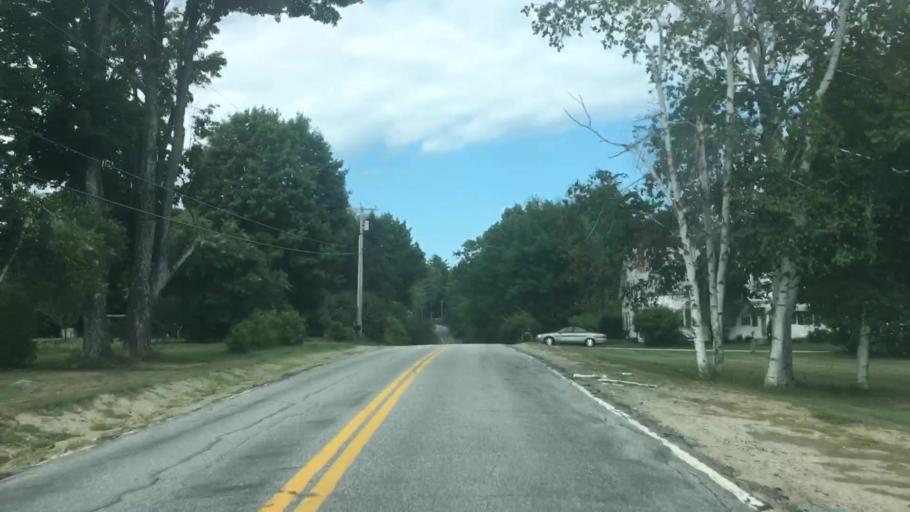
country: US
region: Maine
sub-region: Oxford County
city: Oxford
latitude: 44.0659
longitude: -70.5459
